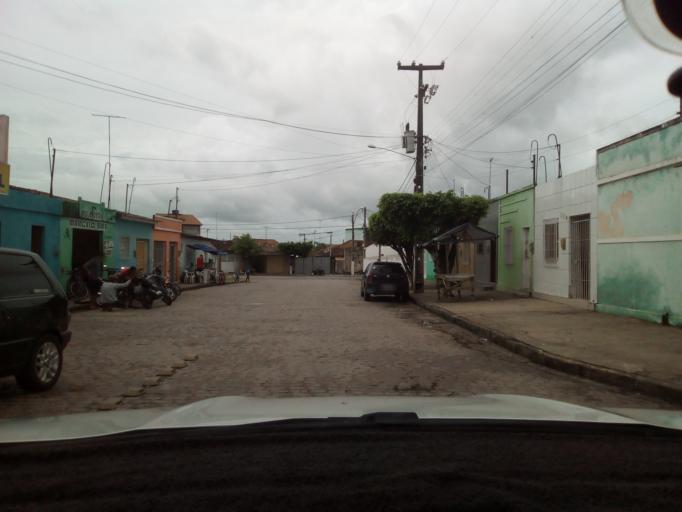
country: BR
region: Paraiba
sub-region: Pedras De Fogo
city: Pedras de Fogo
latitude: -7.4053
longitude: -35.1117
